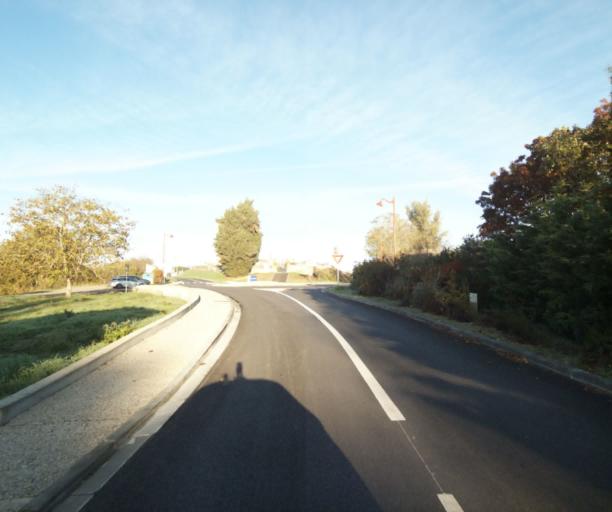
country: FR
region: Midi-Pyrenees
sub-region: Departement de la Haute-Garonne
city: Villemur-sur-Tarn
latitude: 43.9028
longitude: 1.4937
